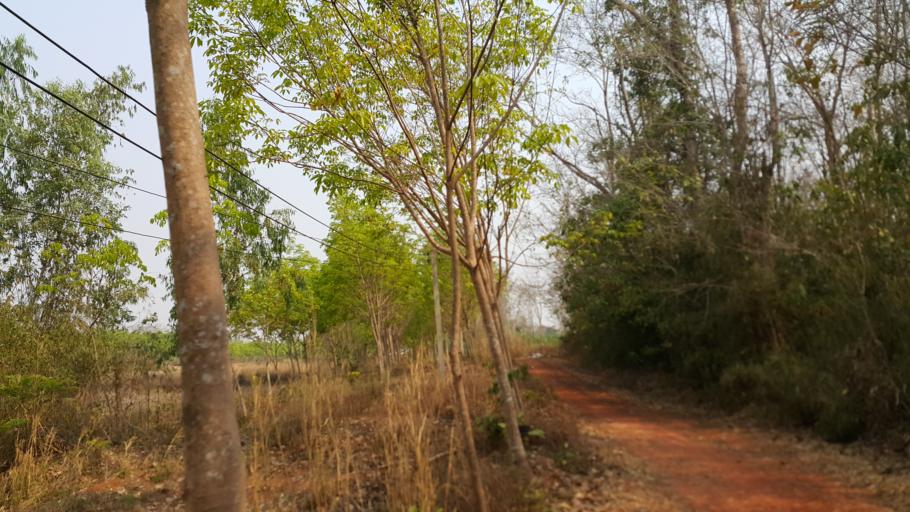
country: TH
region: Nakhon Phanom
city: Ban Phaeng
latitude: 17.8262
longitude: 104.2469
